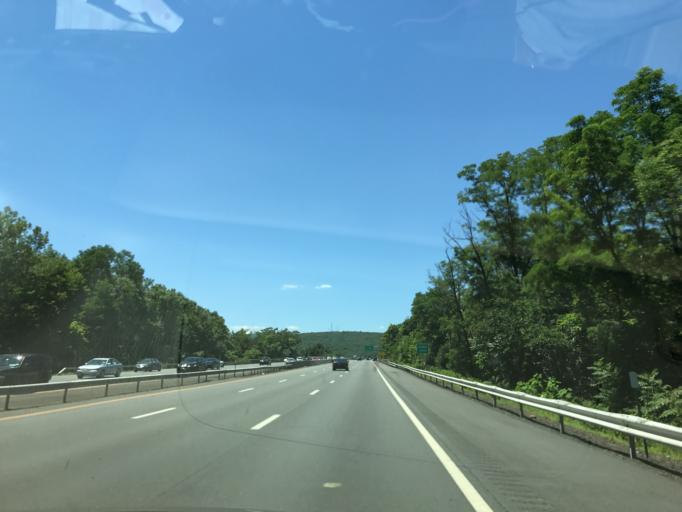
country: US
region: New York
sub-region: Rockland County
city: Suffern
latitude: 41.1210
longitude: -74.1439
